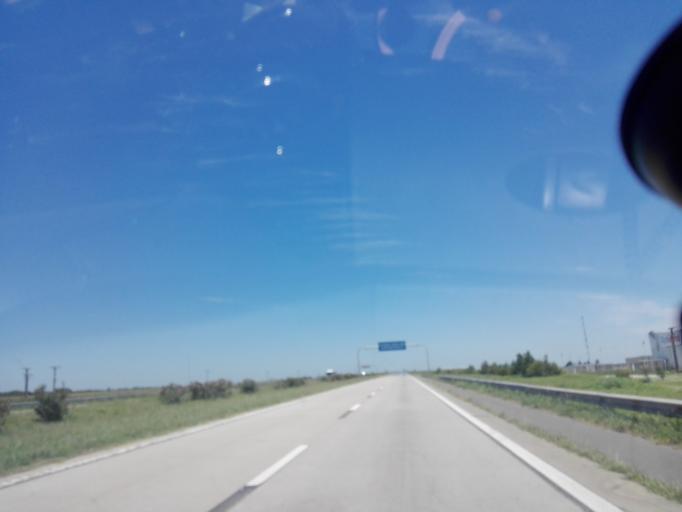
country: AR
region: Cordoba
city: Marcos Juarez
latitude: -32.6667
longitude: -62.0830
